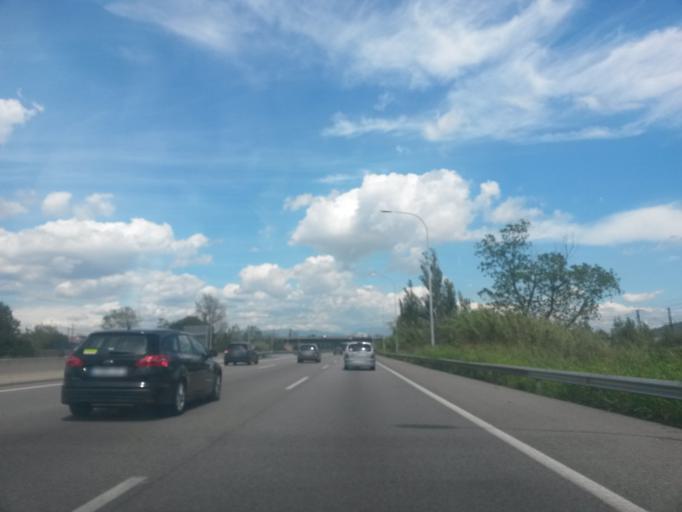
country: ES
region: Catalonia
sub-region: Provincia de Barcelona
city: Mollet del Valles
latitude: 41.5279
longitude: 2.2170
